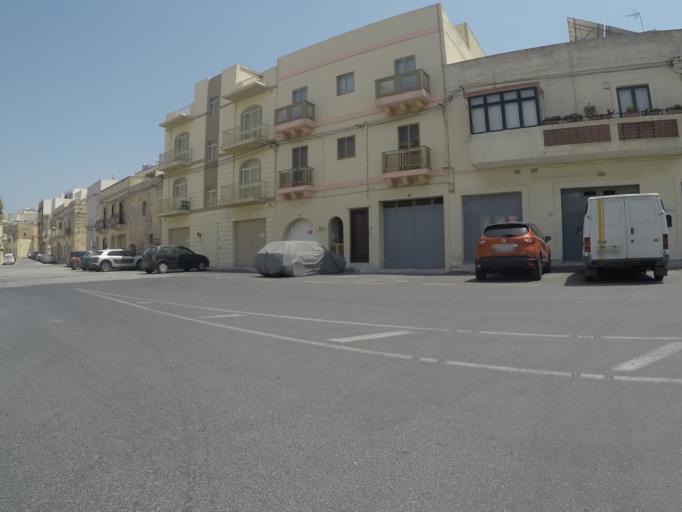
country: MT
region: Ir-Rabat
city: Rabat
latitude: 35.8777
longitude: 14.3957
